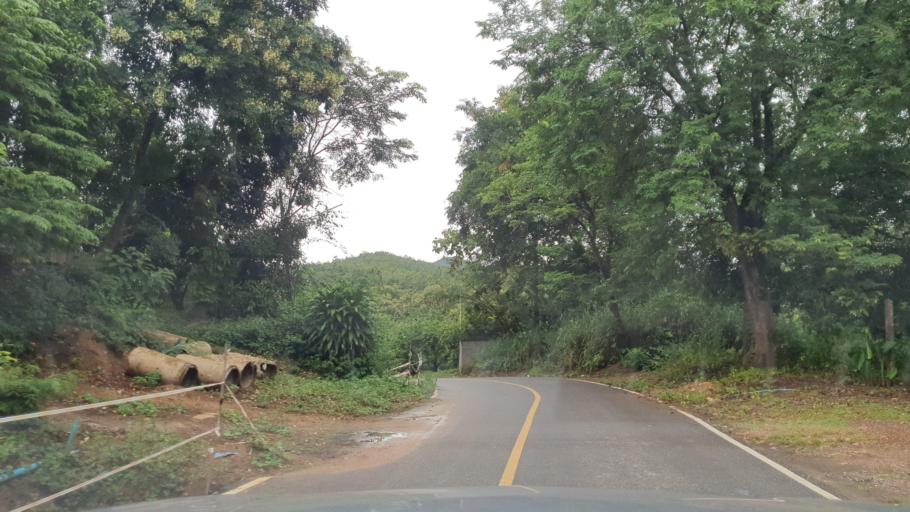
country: TH
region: Chiang Mai
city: Mae Taeng
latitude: 19.1951
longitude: 98.9419
